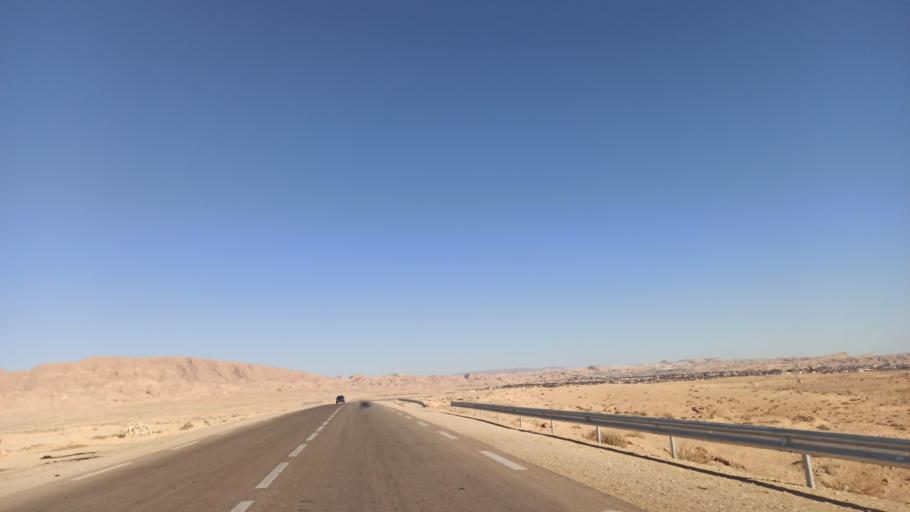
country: TN
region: Gafsa
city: Al Metlaoui
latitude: 34.3001
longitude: 8.3600
